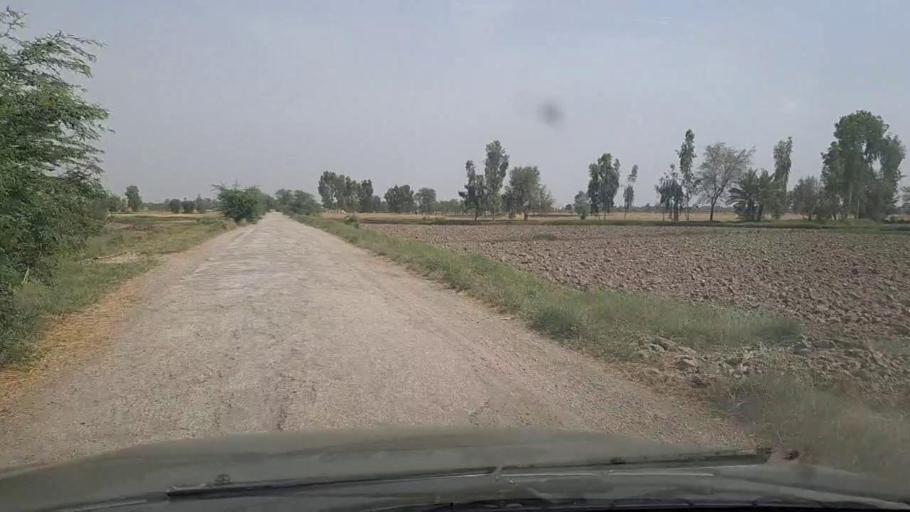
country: PK
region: Sindh
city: Chak
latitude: 27.8367
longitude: 68.7676
